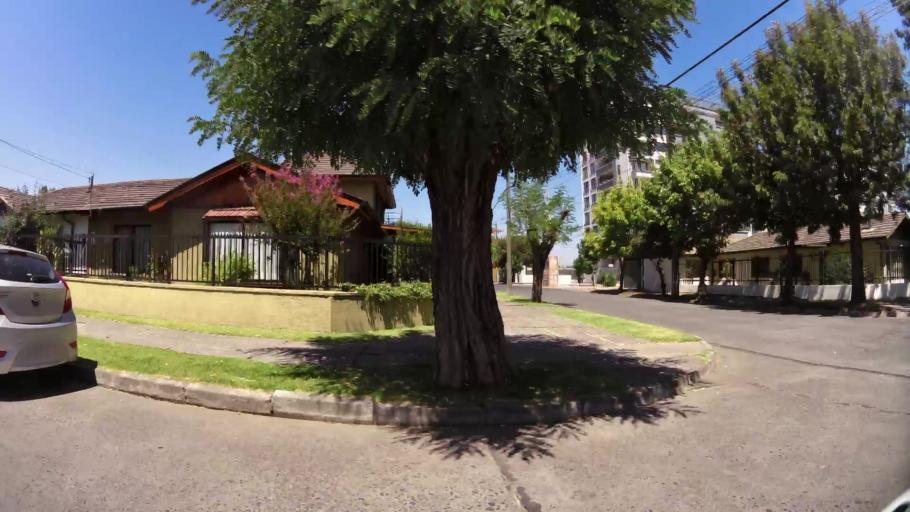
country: CL
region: Maule
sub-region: Provincia de Curico
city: Curico
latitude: -34.9882
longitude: -71.2289
